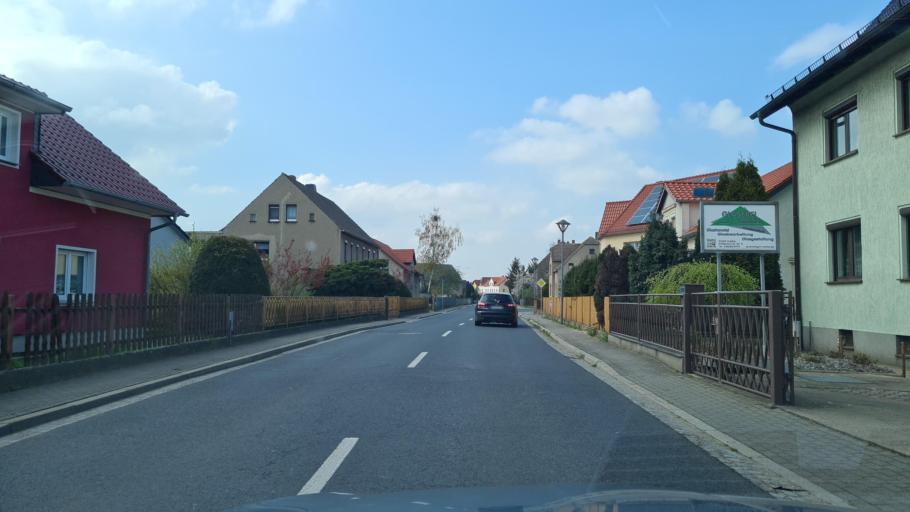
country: DE
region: Saxony
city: Nauwalde
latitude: 51.4075
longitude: 13.4503
